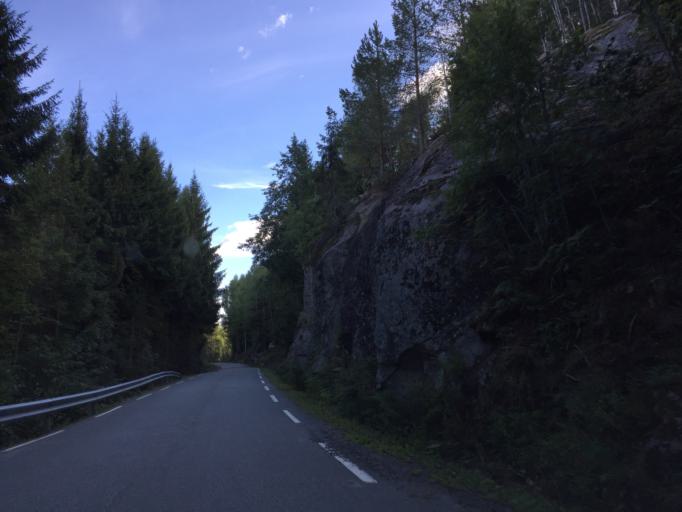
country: NO
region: Buskerud
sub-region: Ovre Eiker
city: Hokksund
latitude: 59.6512
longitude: 9.9164
